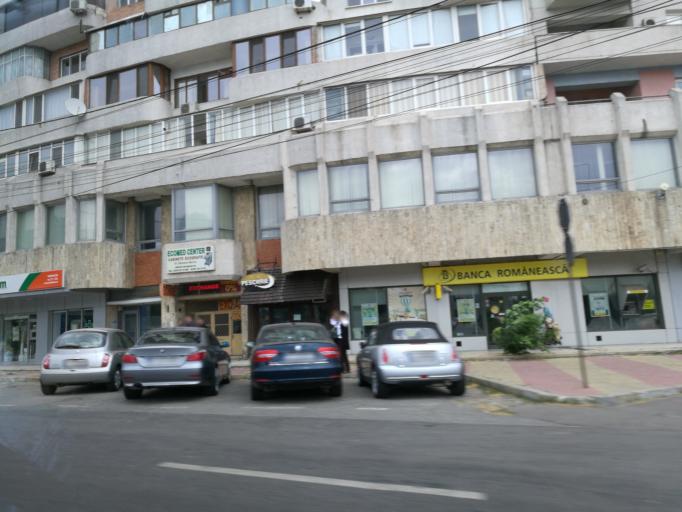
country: RO
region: Constanta
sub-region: Municipiul Constanta
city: Constanta
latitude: 44.1731
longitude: 28.6366
